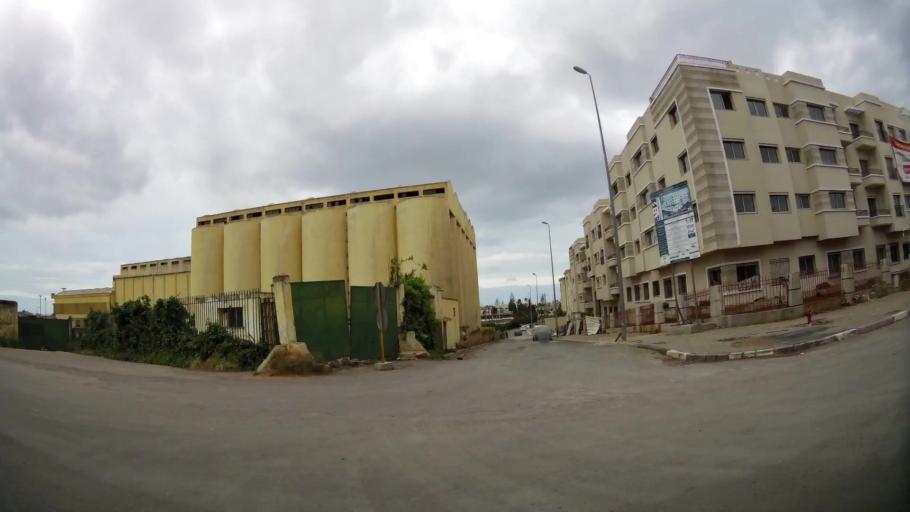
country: MA
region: Grand Casablanca
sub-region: Casablanca
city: Casablanca
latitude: 33.5474
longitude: -7.6398
